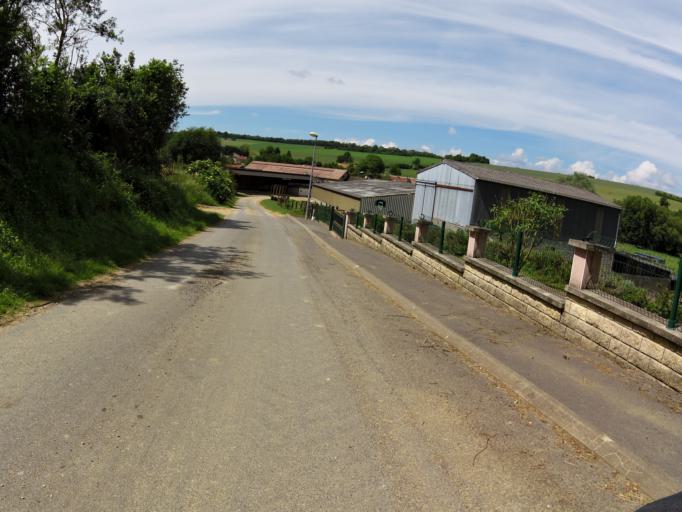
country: FR
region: Champagne-Ardenne
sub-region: Departement des Ardennes
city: Mouzon
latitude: 49.5425
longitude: 5.0836
